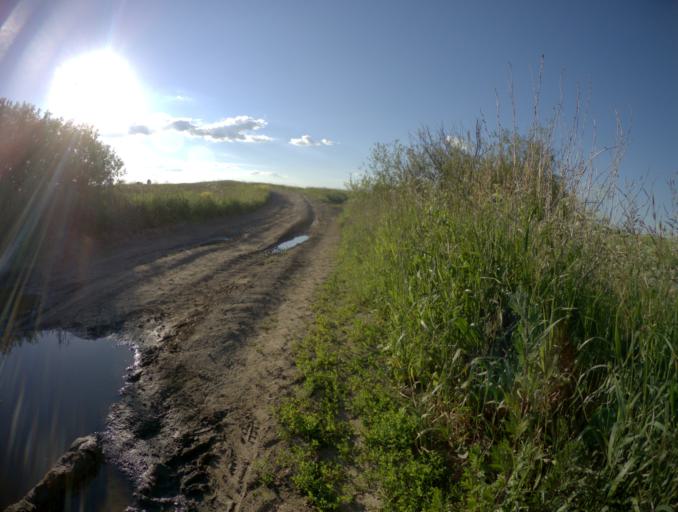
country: RU
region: Vladimir
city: Stavrovo
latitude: 56.2794
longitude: 40.0497
